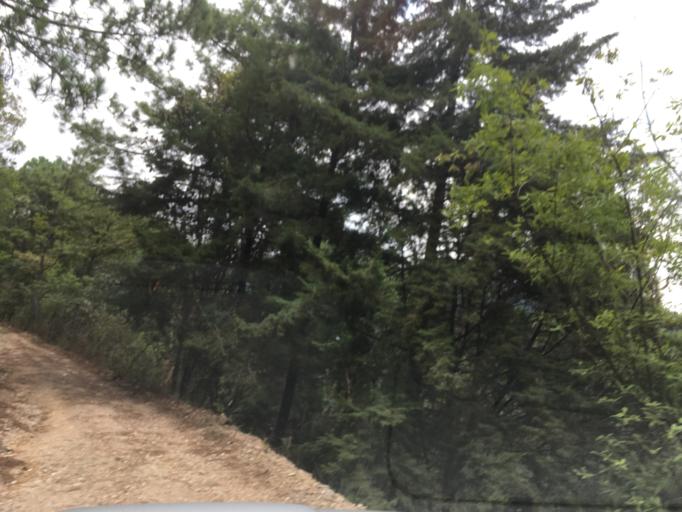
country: MX
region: Michoacan
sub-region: Zitacuaro
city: Macutzio
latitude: 19.5059
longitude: -100.3258
